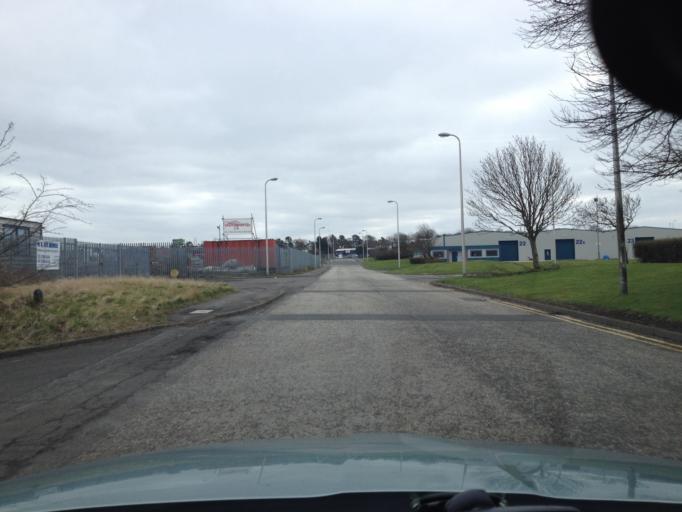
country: GB
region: Scotland
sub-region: West Lothian
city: Livingston
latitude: 55.9076
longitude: -3.5010
